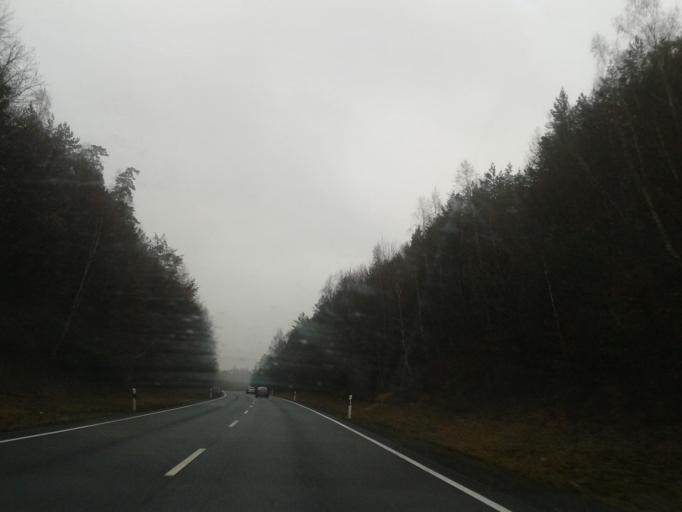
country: DE
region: Bavaria
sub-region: Regierungsbezirk Unterfranken
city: Maroldsweisach
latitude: 50.1625
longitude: 10.6875
